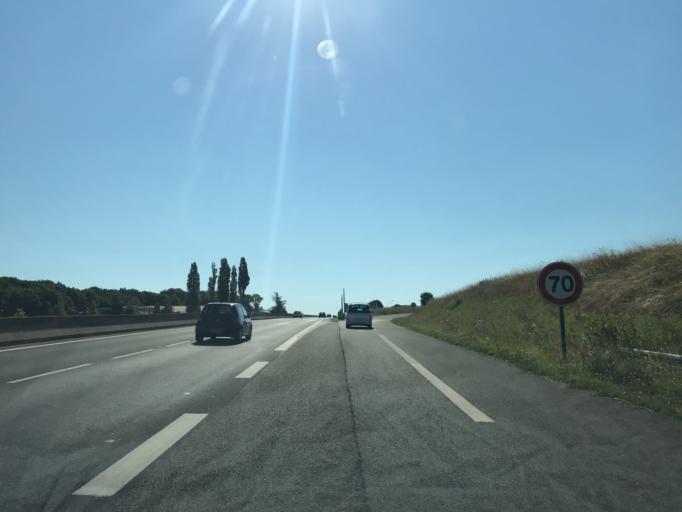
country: FR
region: Ile-de-France
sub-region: Departement du Val-d'Oise
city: Magny-en-Vexin
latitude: 49.1470
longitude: 1.7977
